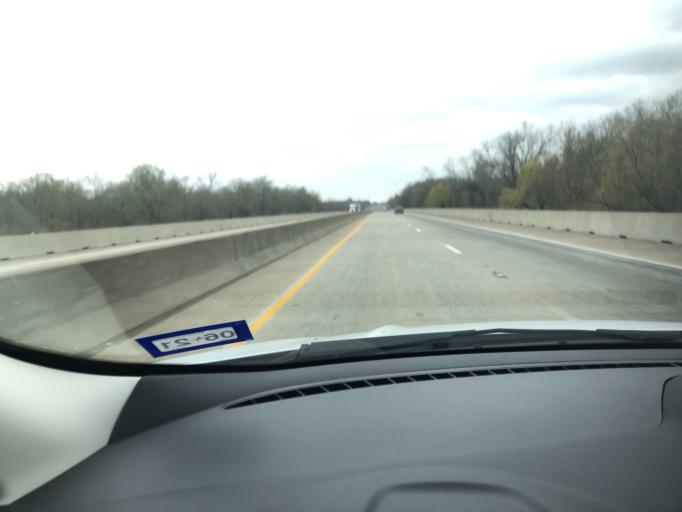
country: US
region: Texas
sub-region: Angelina County
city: Redland
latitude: 31.4601
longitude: -94.7265
